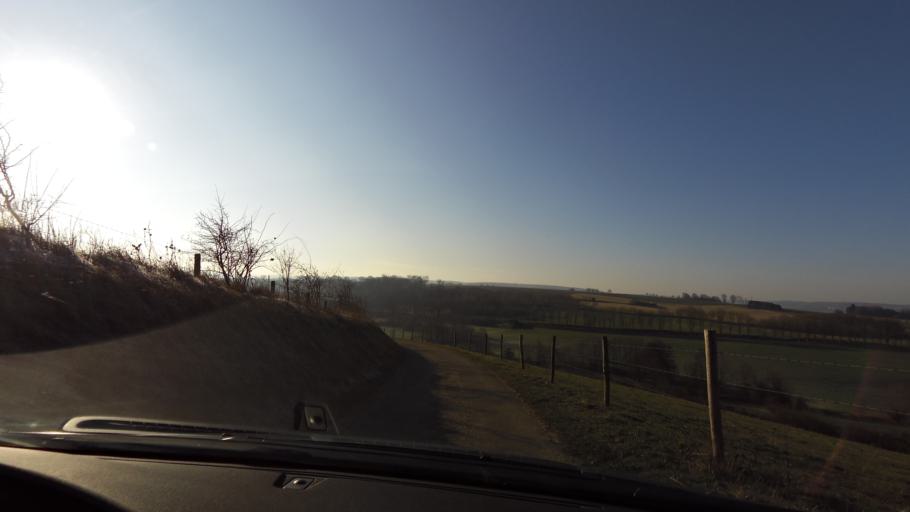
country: NL
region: Limburg
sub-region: Gemeente Voerendaal
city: Ubachsberg
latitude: 50.8141
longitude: 5.9473
